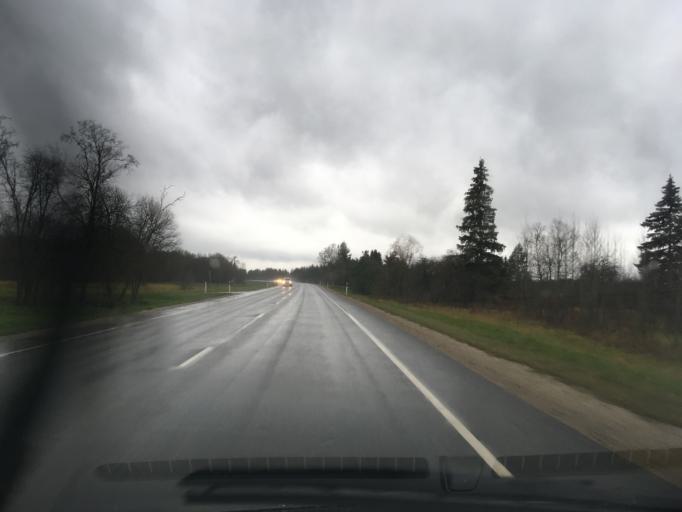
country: EE
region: Laeaene
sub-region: Lihula vald
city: Lihula
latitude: 58.7749
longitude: 23.9905
